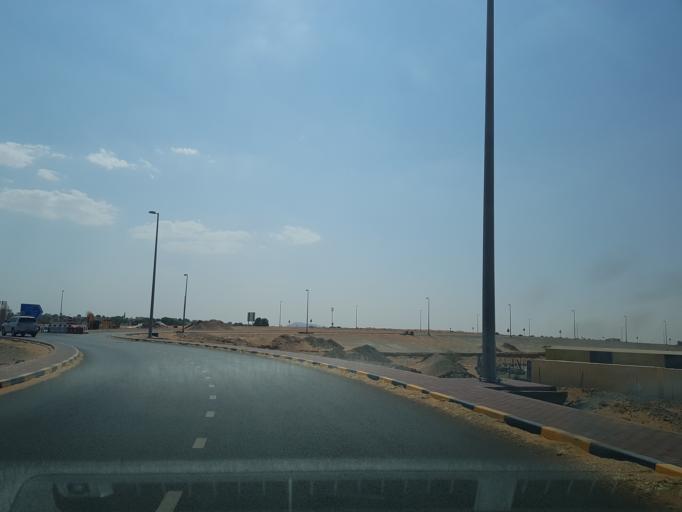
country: AE
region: Ash Shariqah
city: Adh Dhayd
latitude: 25.2330
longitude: 55.9164
